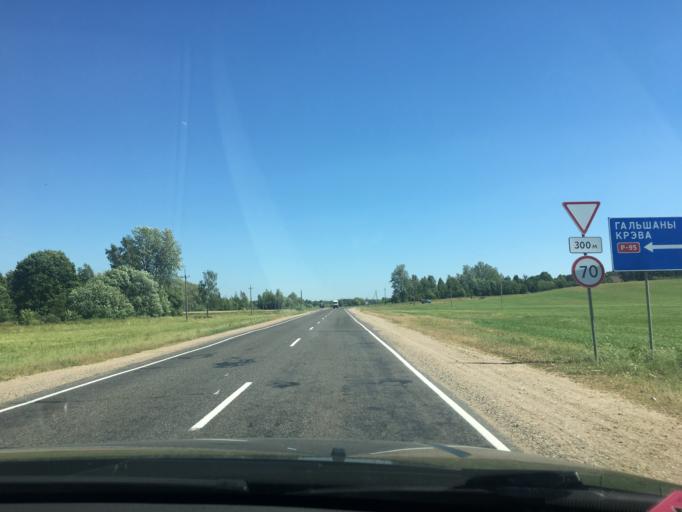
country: BY
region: Grodnenskaya
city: Hal'shany
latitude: 54.2551
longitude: 26.0023
